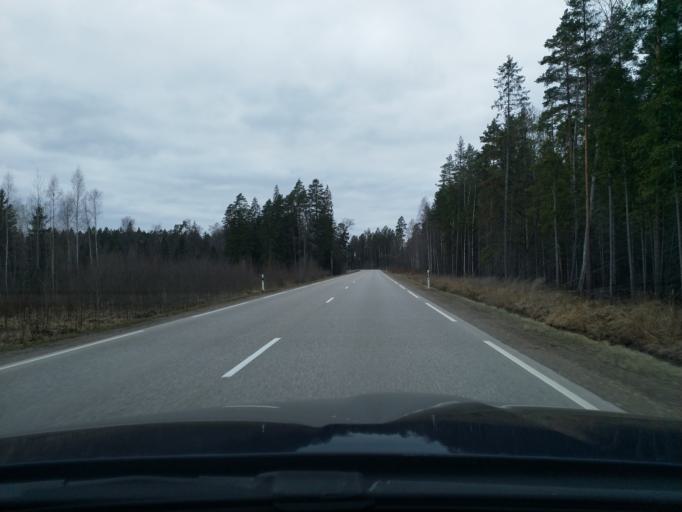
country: LV
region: Kuldigas Rajons
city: Kuldiga
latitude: 56.9551
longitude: 22.1388
